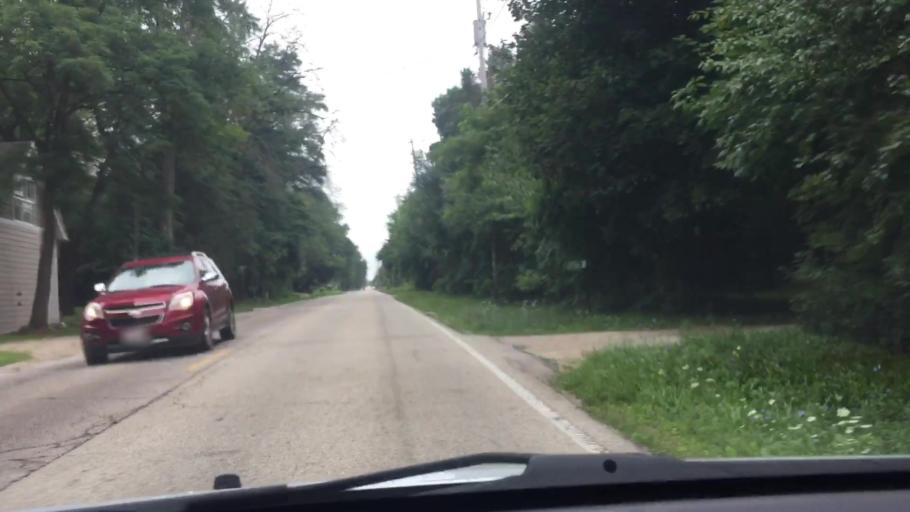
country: US
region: Wisconsin
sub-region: Waukesha County
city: Delafield
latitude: 43.0550
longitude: -88.4424
